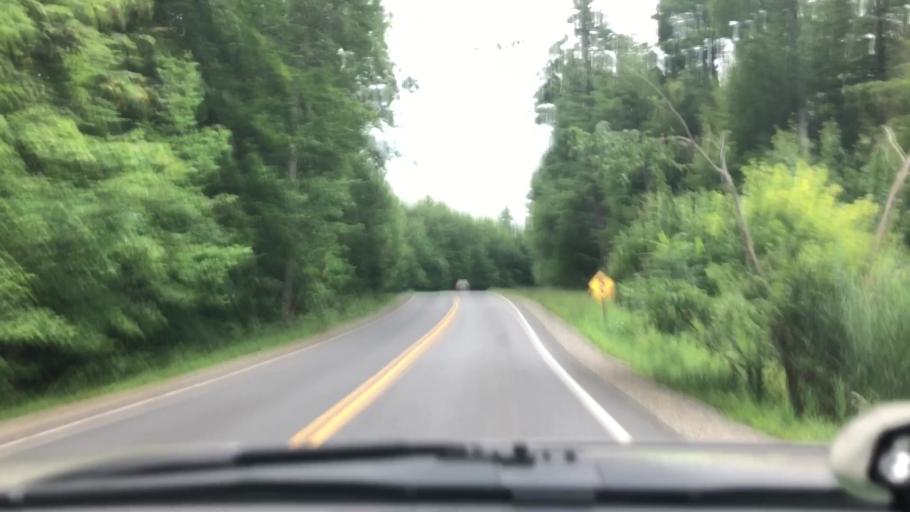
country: US
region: New York
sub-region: Saratoga County
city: Corinth
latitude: 43.1999
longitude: -73.7634
